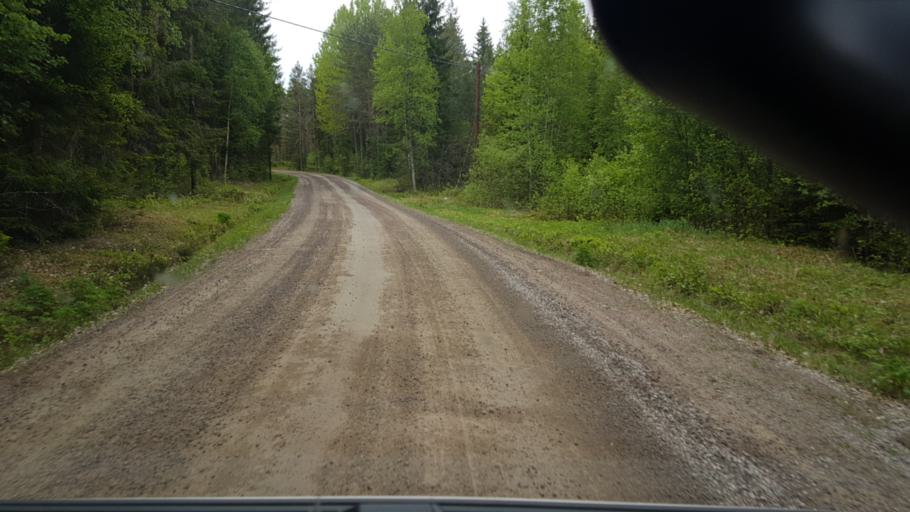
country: SE
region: Vaermland
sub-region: Arvika Kommun
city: Arvika
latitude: 59.5214
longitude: 12.7332
